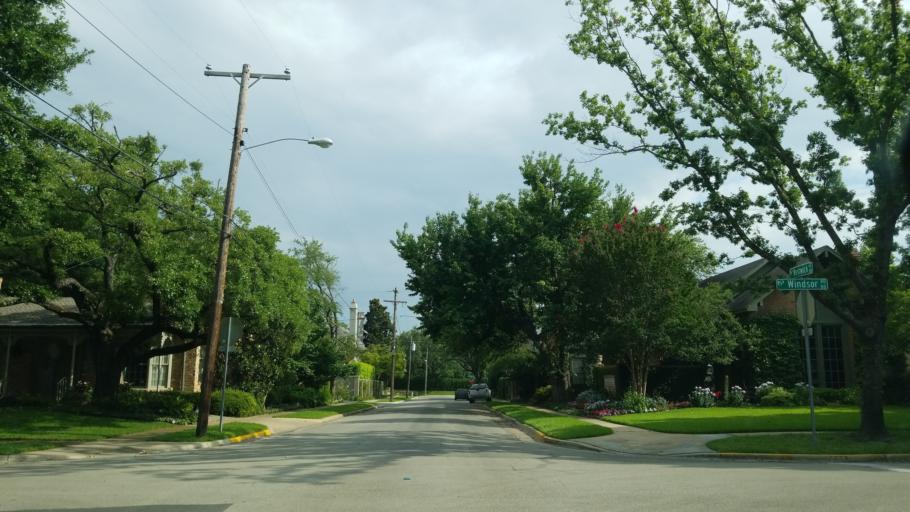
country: US
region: Texas
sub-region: Dallas County
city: University Park
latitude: 32.8432
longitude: -96.8020
